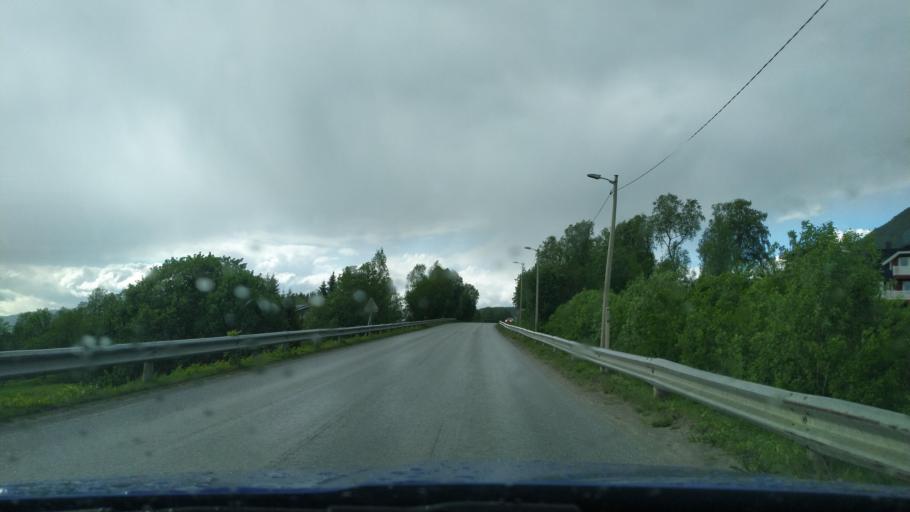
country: NO
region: Troms
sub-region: Sorreisa
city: Sorreisa
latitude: 69.1522
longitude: 18.1675
